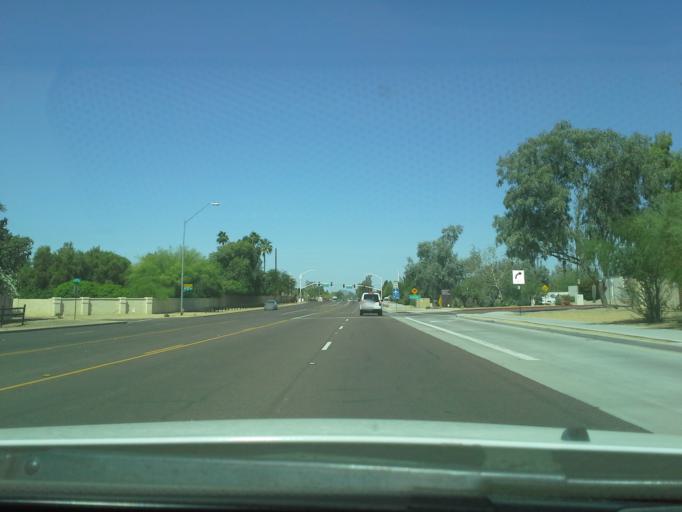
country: US
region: Arizona
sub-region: Maricopa County
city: Paradise Valley
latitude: 33.5968
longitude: -111.9232
